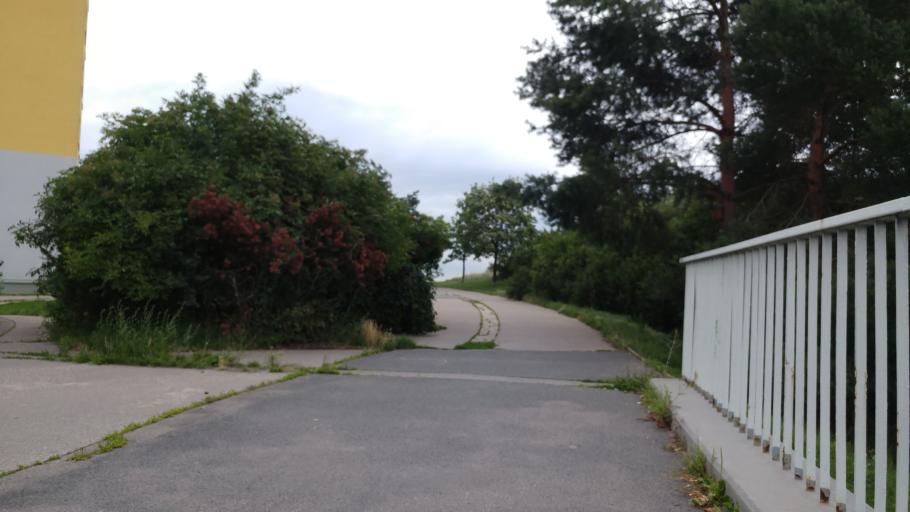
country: CZ
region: Praha
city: Branik
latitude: 50.0473
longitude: 14.3411
